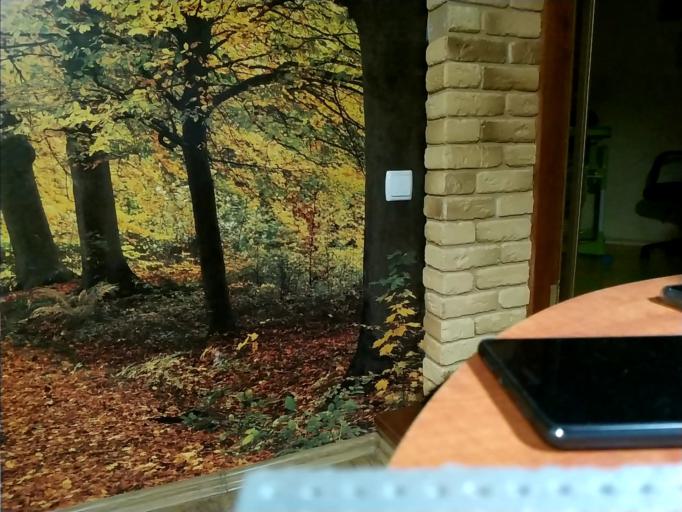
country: RU
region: Tverskaya
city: Zubtsov
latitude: 56.2870
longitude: 34.6886
